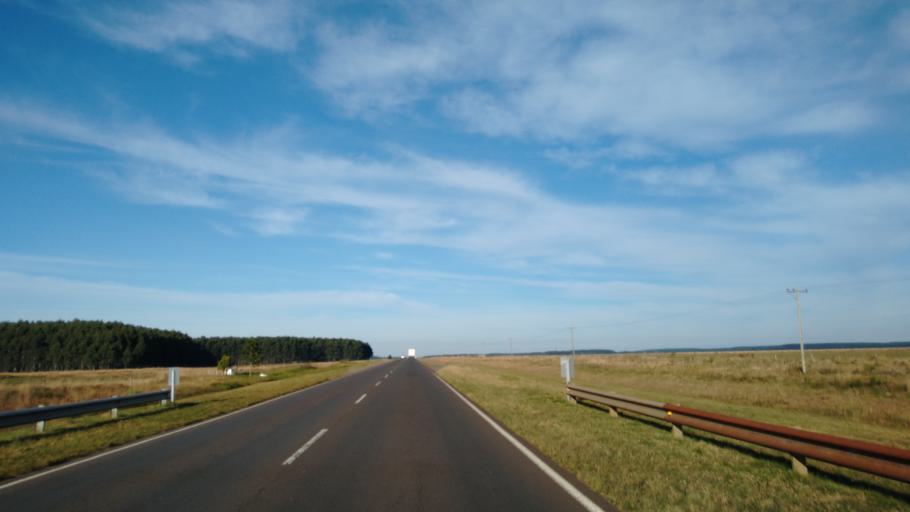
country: AR
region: Corrientes
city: Yapeyu
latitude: -29.3056
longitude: -56.7768
